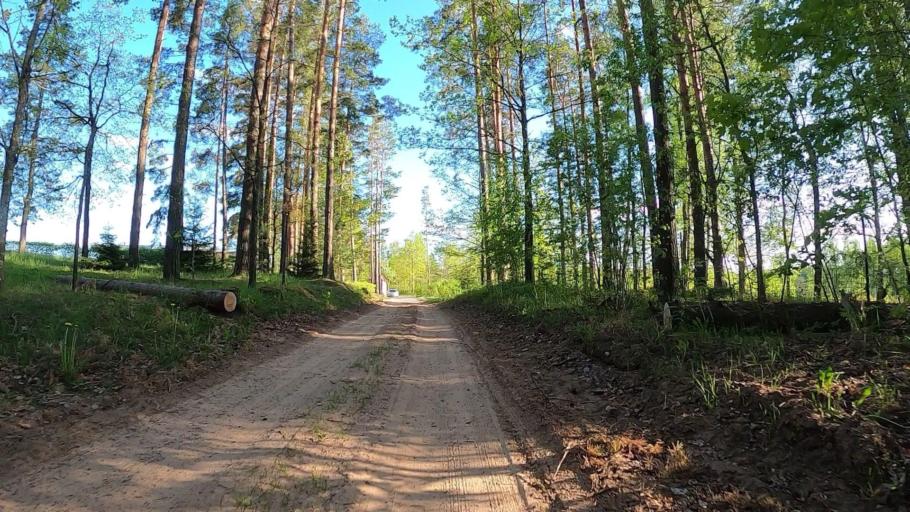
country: LV
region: Baldone
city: Baldone
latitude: 56.7723
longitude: 24.3347
